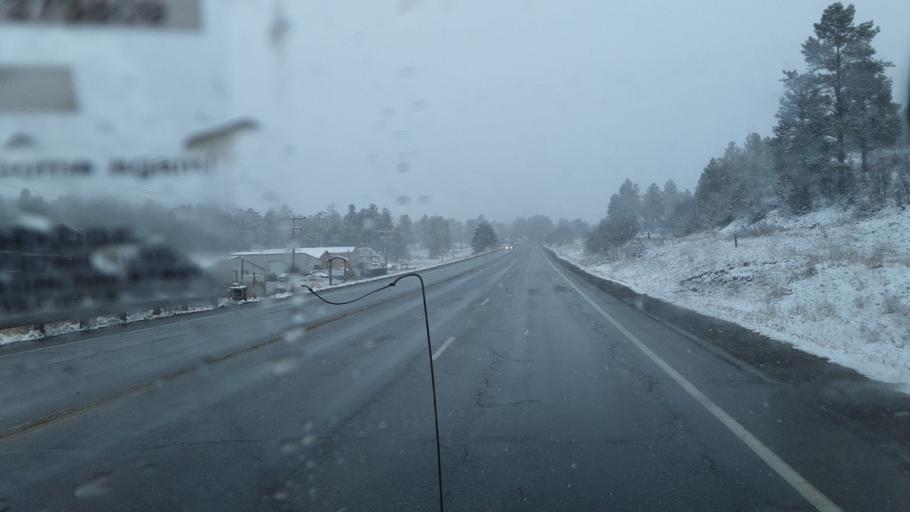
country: US
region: Colorado
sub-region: Archuleta County
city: Pagosa Springs
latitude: 37.2694
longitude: -107.0302
